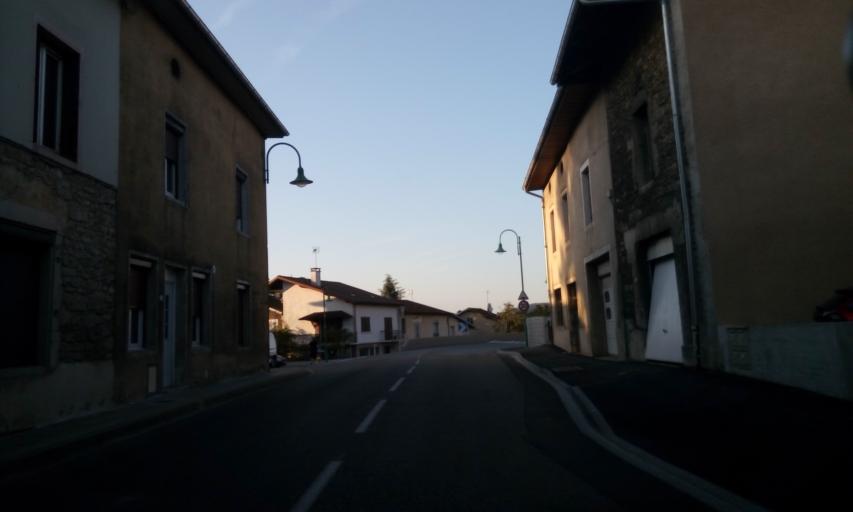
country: FR
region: Rhone-Alpes
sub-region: Departement de l'Ain
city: Saint-Martin-du-Frene
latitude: 46.1415
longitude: 5.5532
